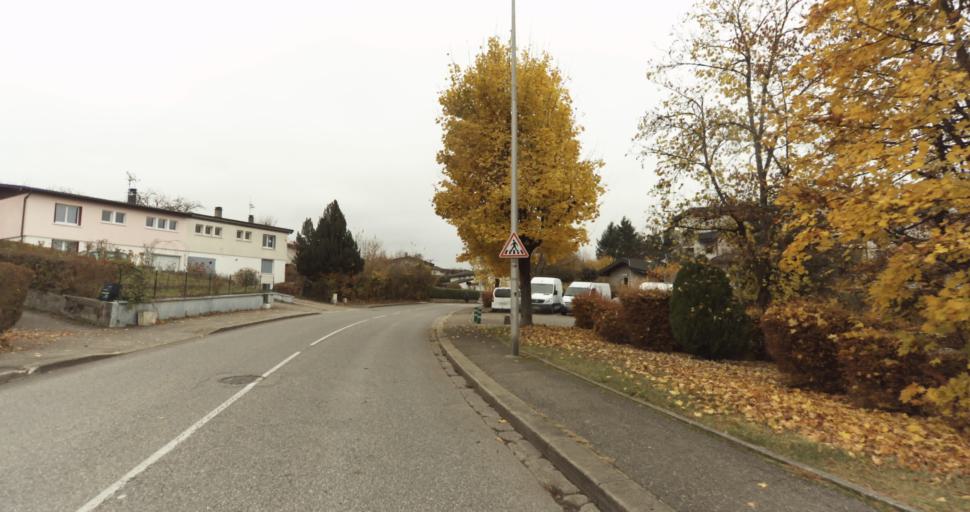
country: FR
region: Rhone-Alpes
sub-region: Departement de la Haute-Savoie
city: Cran-Gevrier
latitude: 45.9018
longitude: 6.0957
